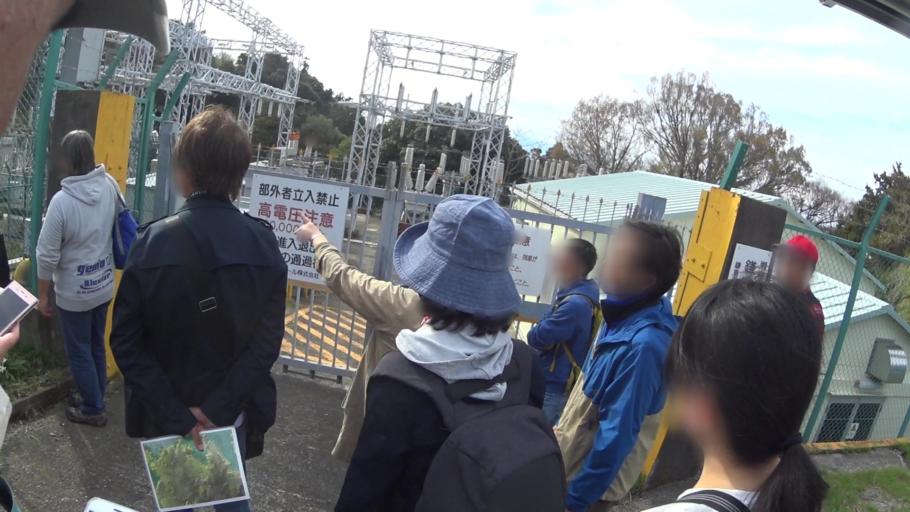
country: JP
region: Kanagawa
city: Kamakura
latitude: 35.3260
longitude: 139.5143
